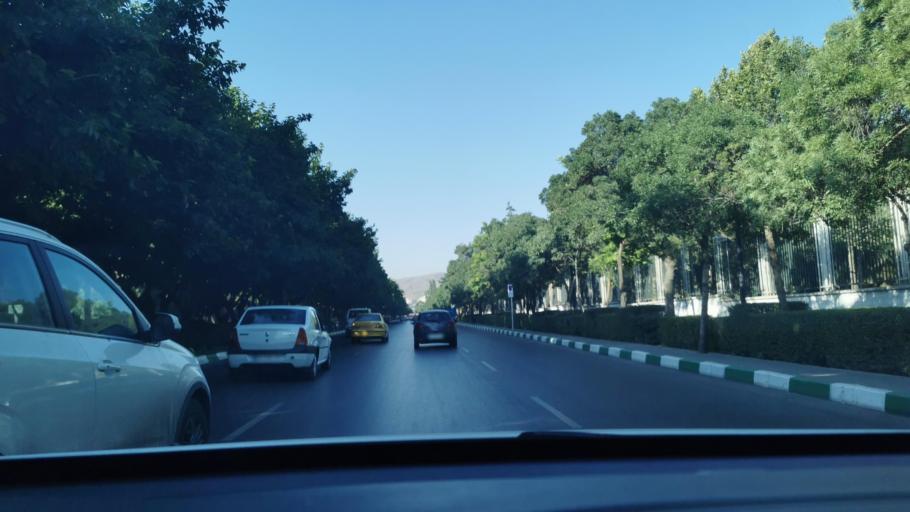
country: IR
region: Razavi Khorasan
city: Mashhad
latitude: 36.2976
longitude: 59.5618
